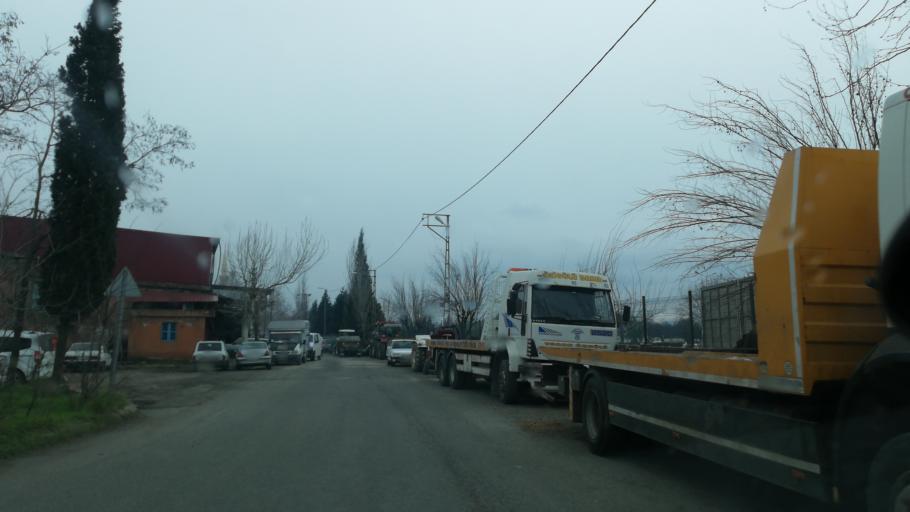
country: TR
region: Kahramanmaras
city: Kahramanmaras
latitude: 37.5589
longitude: 36.9563
